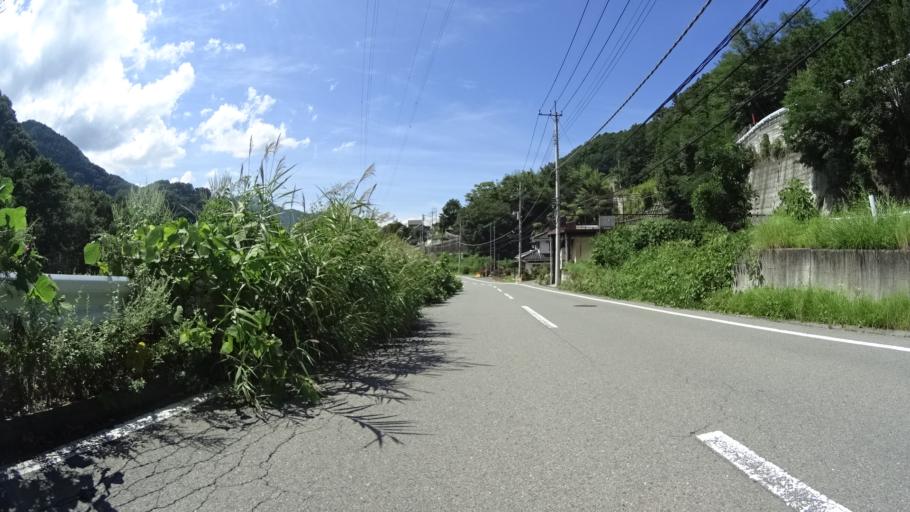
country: JP
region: Yamanashi
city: Enzan
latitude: 35.6400
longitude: 138.7967
